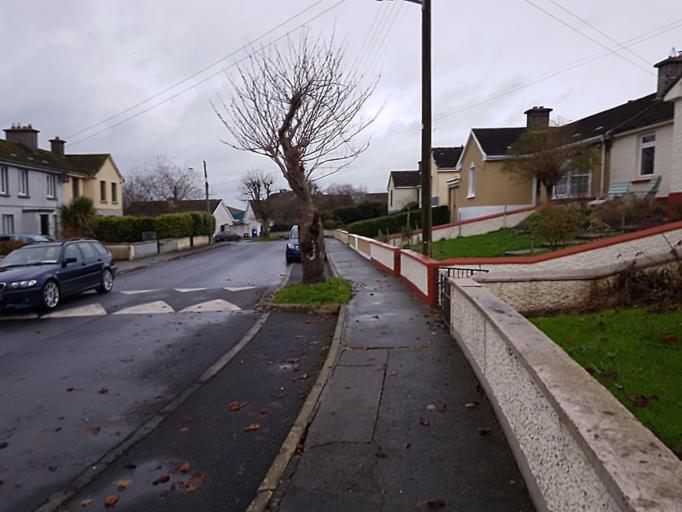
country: IE
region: Leinster
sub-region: Kilkenny
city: Kilkenny
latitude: 52.6542
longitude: -7.2371
